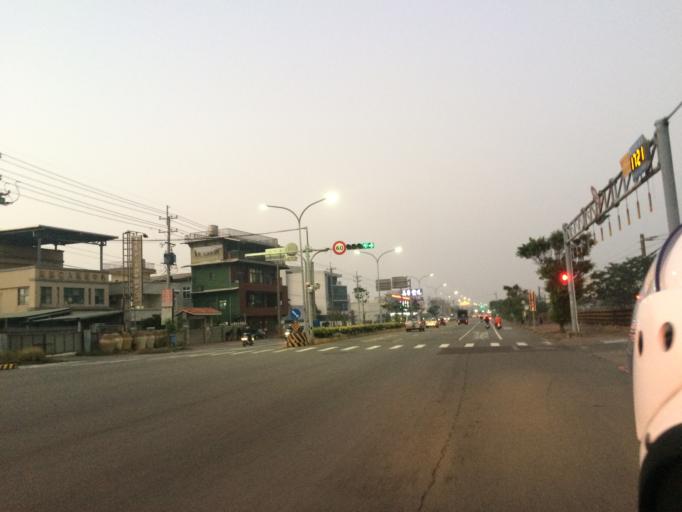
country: TW
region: Taiwan
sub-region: Hsinchu
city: Hsinchu
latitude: 24.7781
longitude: 120.9187
